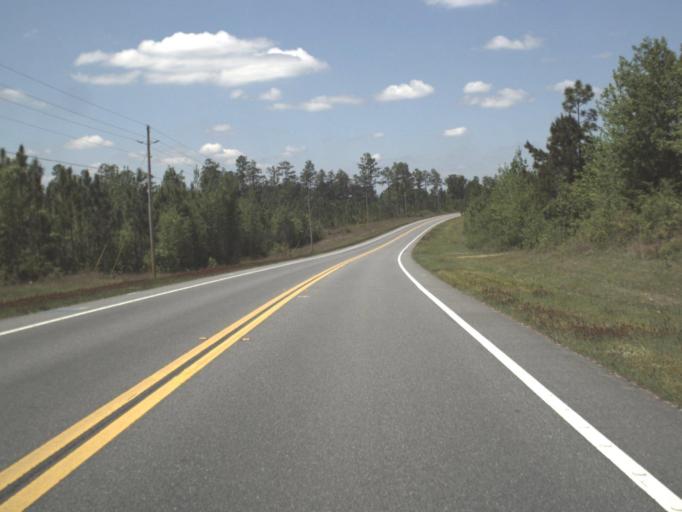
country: US
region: Alabama
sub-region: Escambia County
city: East Brewton
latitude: 30.9576
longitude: -87.0437
